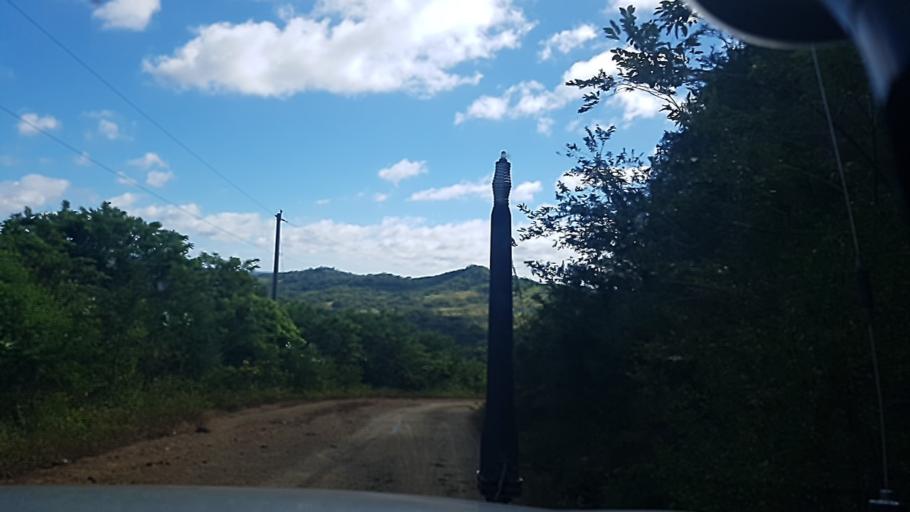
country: NI
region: Carazo
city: Santa Teresa
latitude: 11.6108
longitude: -86.1526
